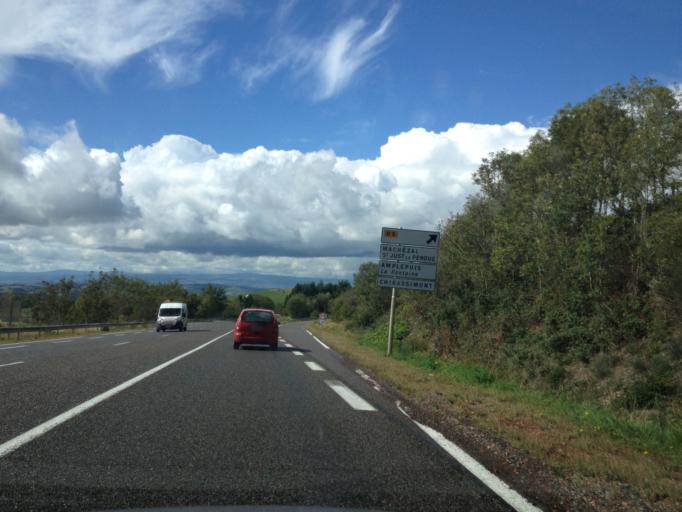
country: FR
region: Rhone-Alpes
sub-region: Departement du Rhone
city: Amplepuis
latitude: 45.9215
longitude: 4.3174
